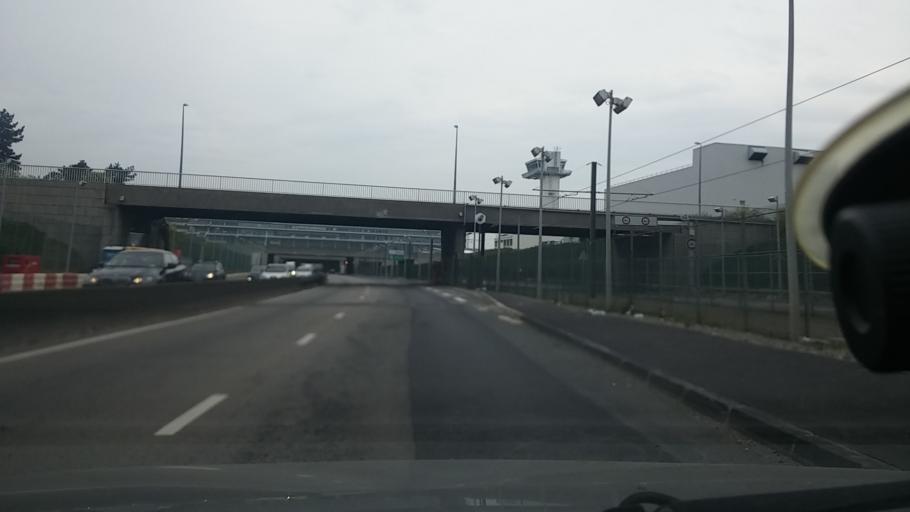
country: FR
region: Ile-de-France
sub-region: Departement de l'Essonne
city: Paray-Vieille-Poste
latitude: 48.7229
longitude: 2.3706
